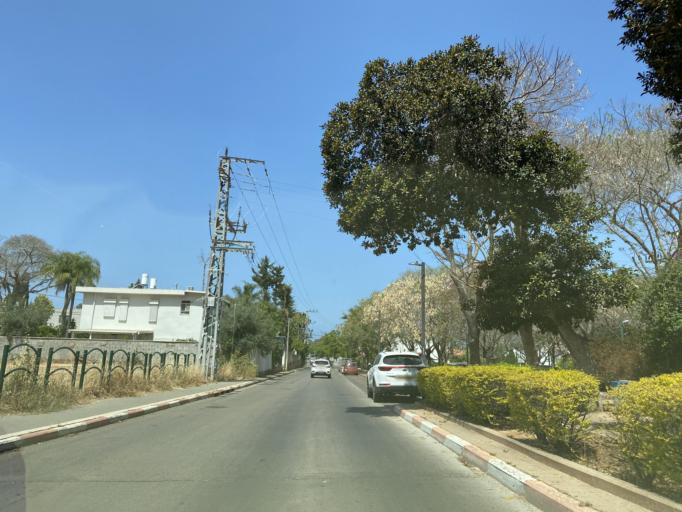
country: IL
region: Tel Aviv
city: Ramat HaSharon
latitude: 32.1528
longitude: 34.8391
